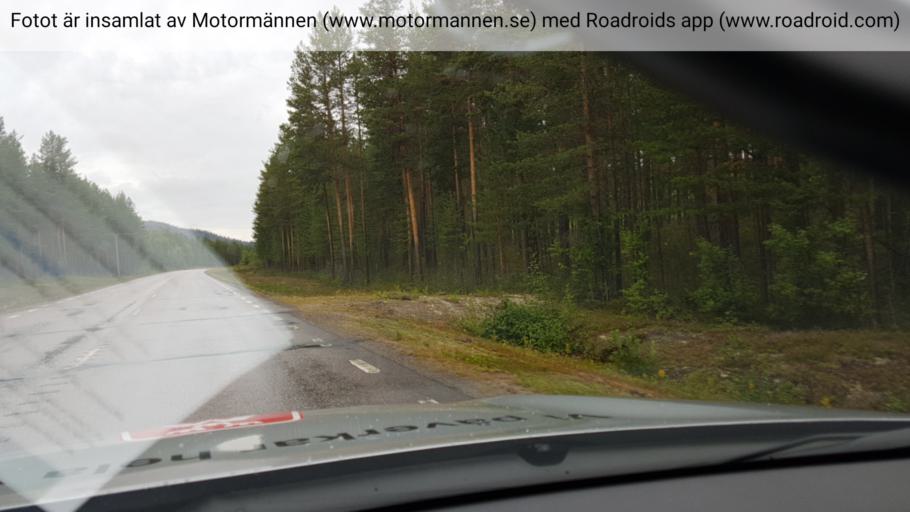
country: SE
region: Norrbotten
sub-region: Alvsbyns Kommun
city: AElvsbyn
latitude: 66.1392
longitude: 20.8879
